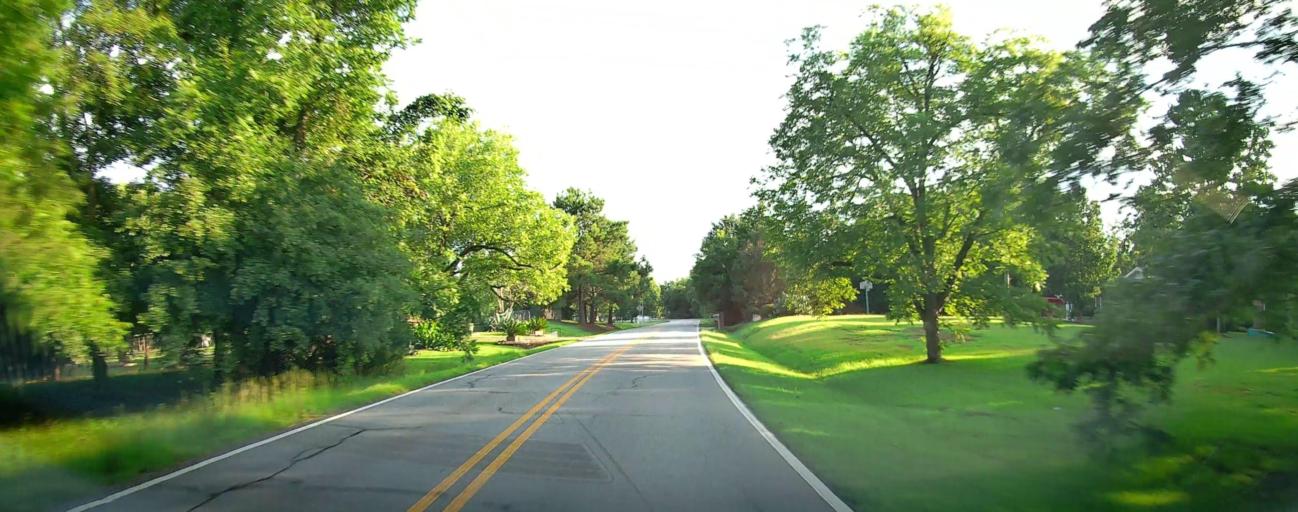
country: US
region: Georgia
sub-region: Peach County
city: Fort Valley
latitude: 32.5894
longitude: -83.8727
